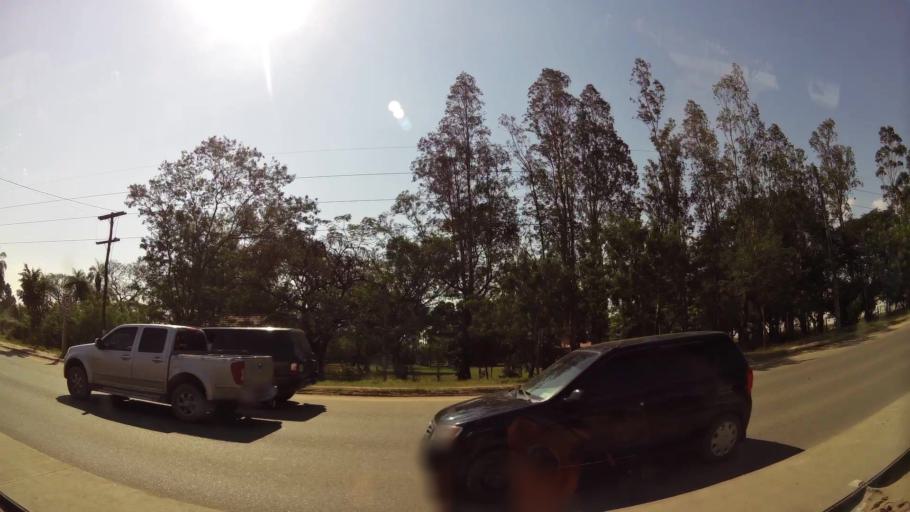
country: BO
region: Santa Cruz
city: Cotoca
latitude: -17.7644
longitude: -63.1012
